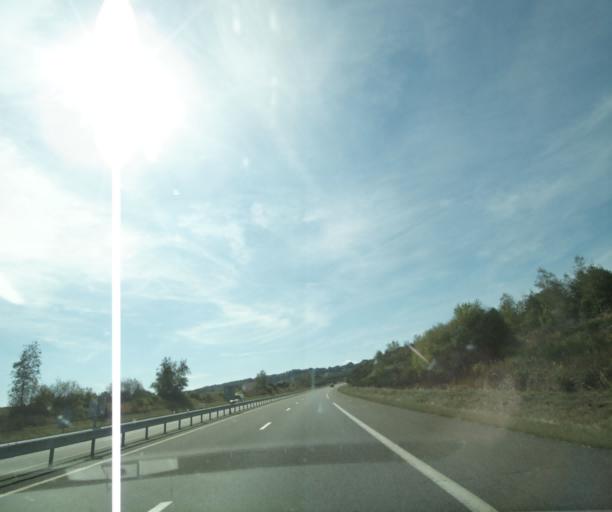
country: FR
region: Auvergne
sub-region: Departement du Puy-de-Dome
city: Chapdes-Beaufort
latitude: 45.8395
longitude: 2.8276
